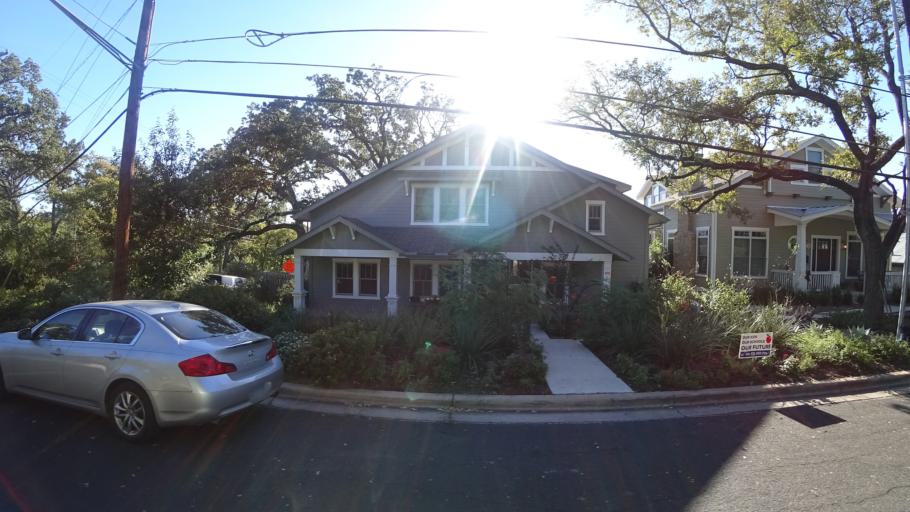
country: US
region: Texas
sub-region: Travis County
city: Rollingwood
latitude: 30.2846
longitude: -97.7668
